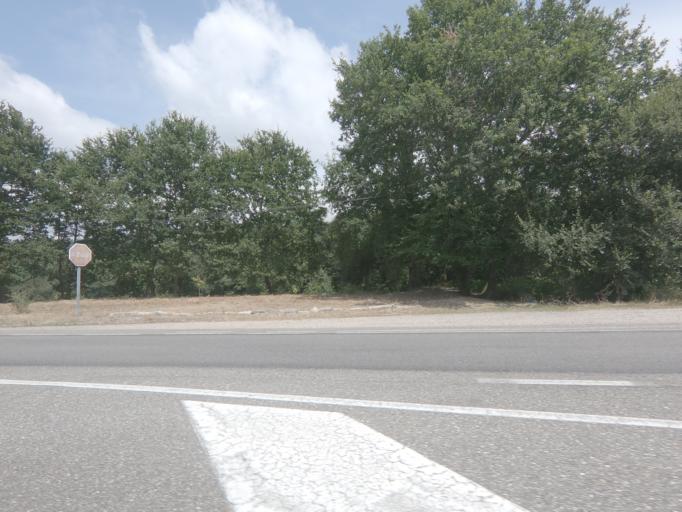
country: ES
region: Galicia
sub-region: Provincia de Pontevedra
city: Tomino
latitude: 42.0266
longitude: -8.7327
